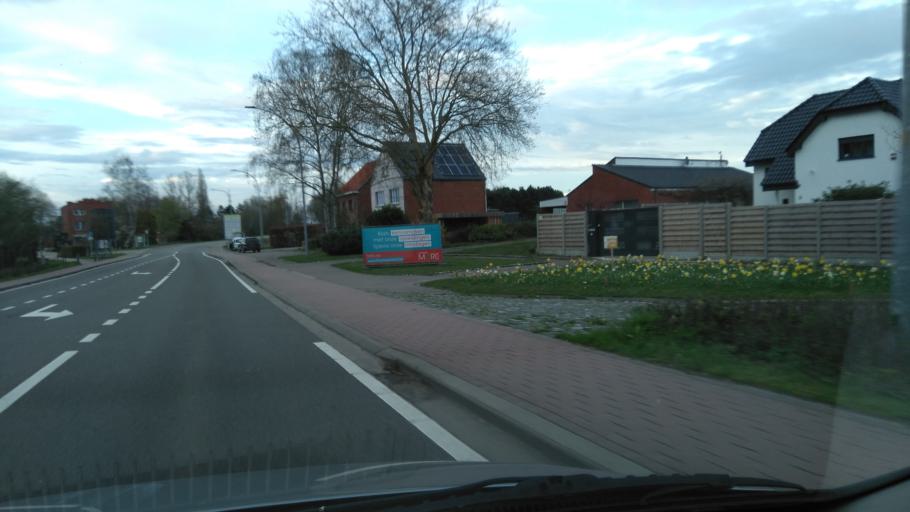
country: BE
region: Flanders
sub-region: Provincie Antwerpen
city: Laakdal
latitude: 51.1192
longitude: 4.9791
